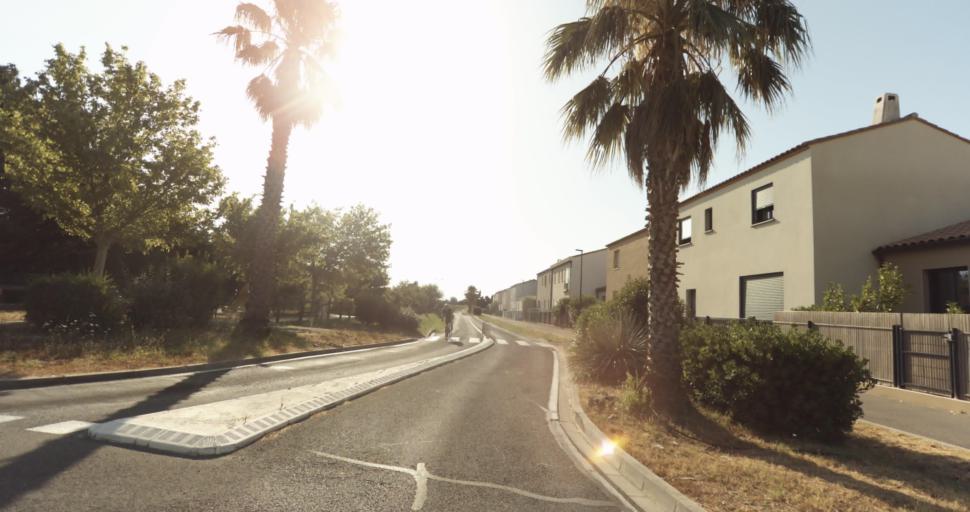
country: FR
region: Languedoc-Roussillon
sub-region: Departement des Pyrenees-Orientales
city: Alenya
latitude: 42.6382
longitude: 2.9885
